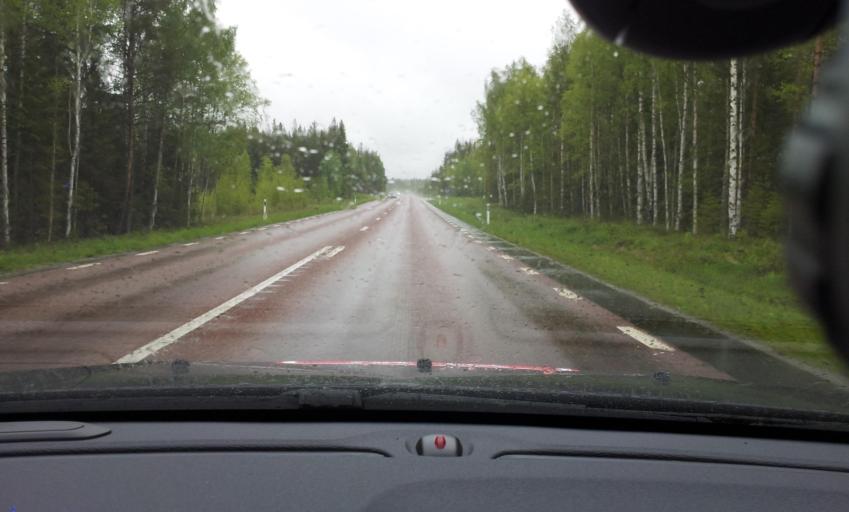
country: SE
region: Jaemtland
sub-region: Bergs Kommun
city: Hoverberg
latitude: 62.8272
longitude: 14.5176
